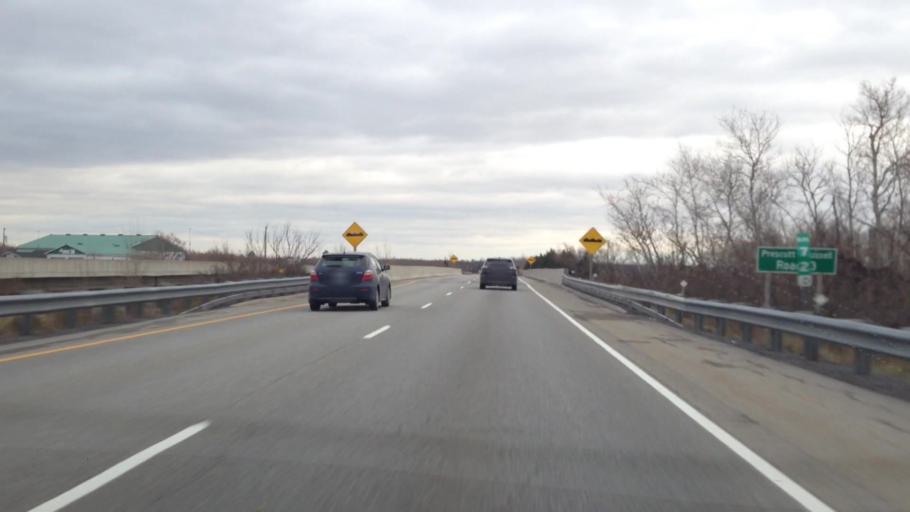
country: CA
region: Ontario
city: Casselman
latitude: 45.3112
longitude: -75.1531
